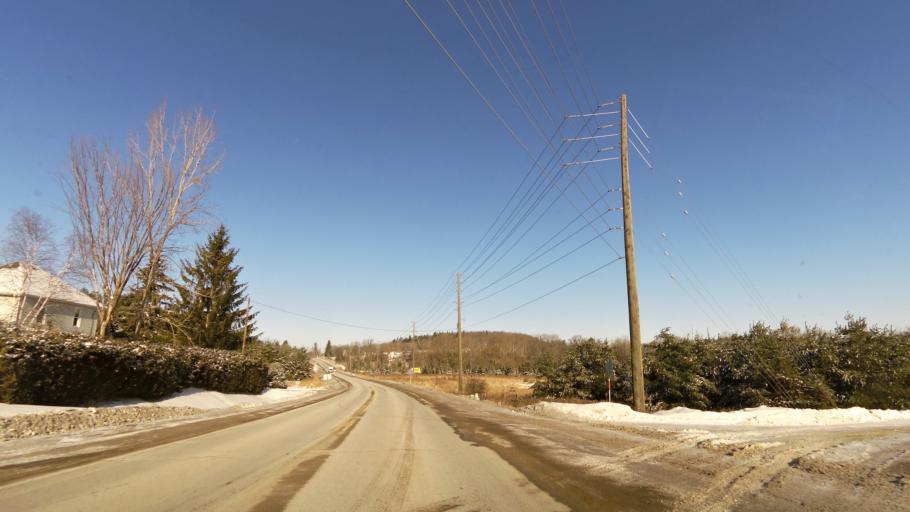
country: CA
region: Ontario
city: Quinte West
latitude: 44.1962
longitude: -77.8170
